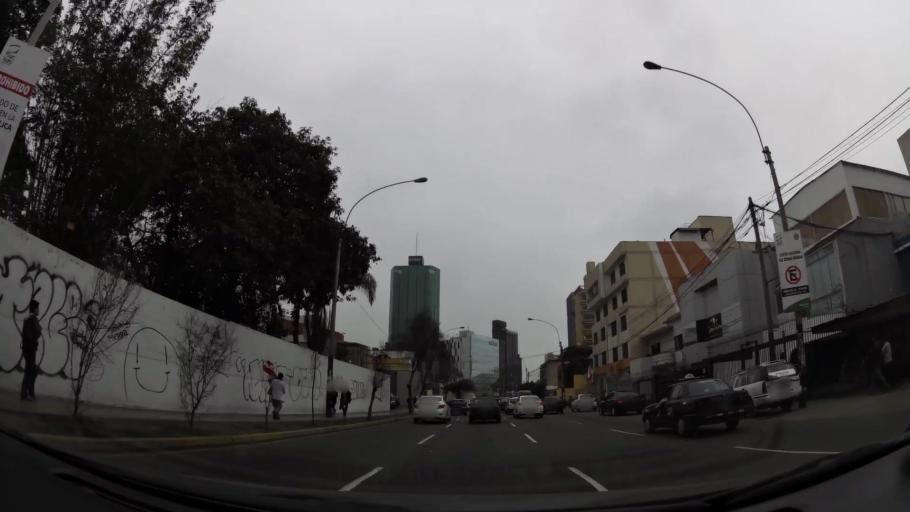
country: PE
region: Lima
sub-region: Lima
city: San Isidro
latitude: -12.0910
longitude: -77.0347
